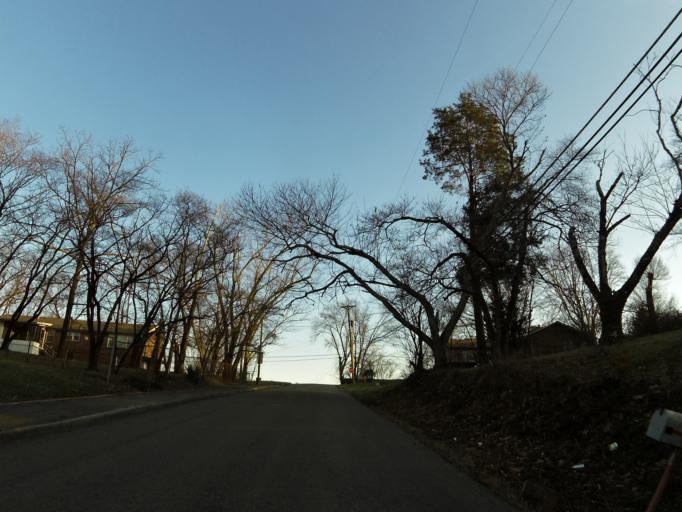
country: US
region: Tennessee
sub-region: Knox County
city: Knoxville
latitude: 36.0171
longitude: -83.8861
